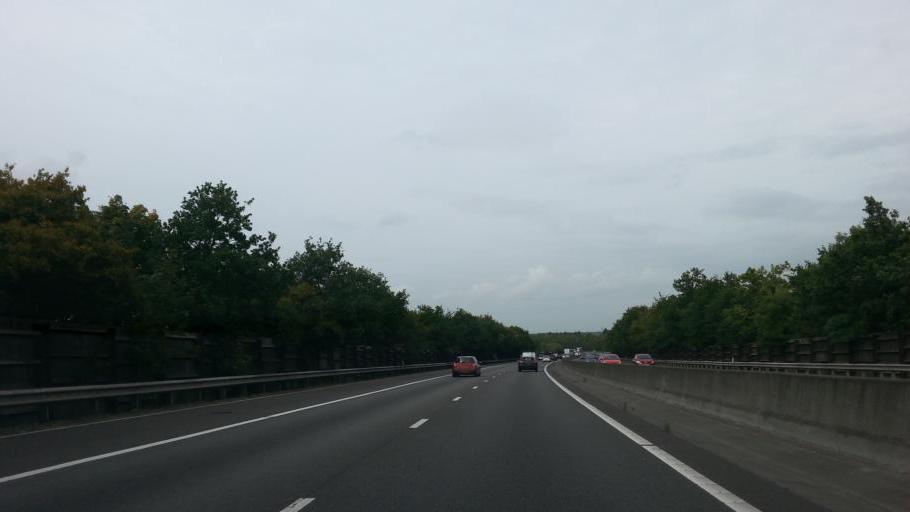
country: GB
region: England
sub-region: Essex
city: Elsenham
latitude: 51.9227
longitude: 0.2203
